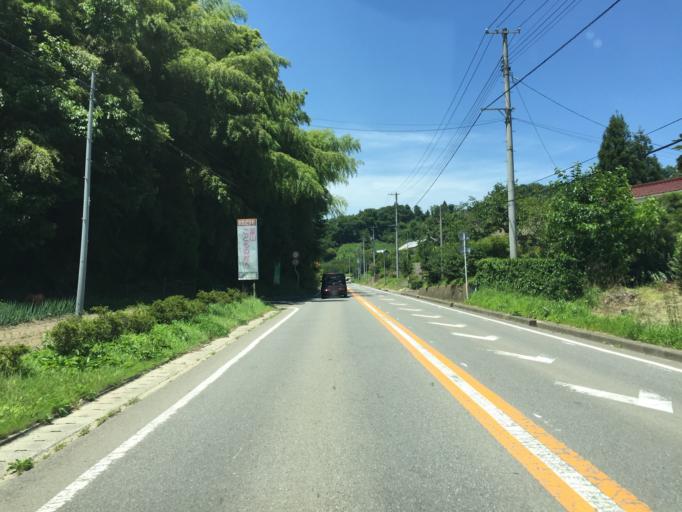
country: JP
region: Fukushima
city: Hobaramachi
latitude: 37.7743
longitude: 140.6086
